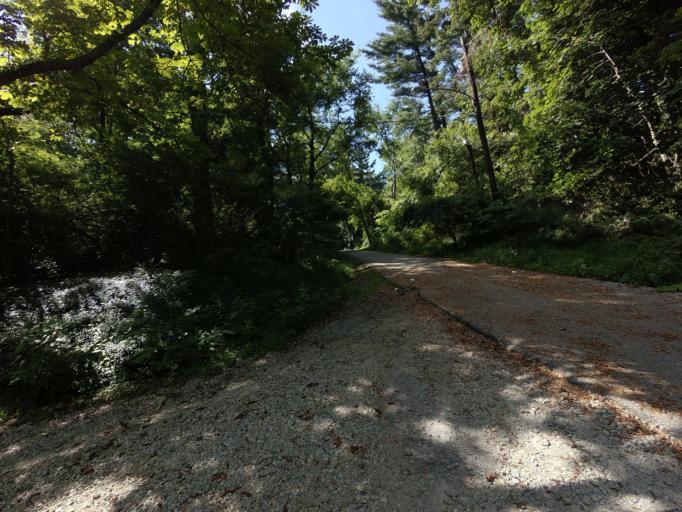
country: US
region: Pennsylvania
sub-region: Montgomery County
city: Bala-Cynwyd
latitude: 40.0249
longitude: -75.2001
